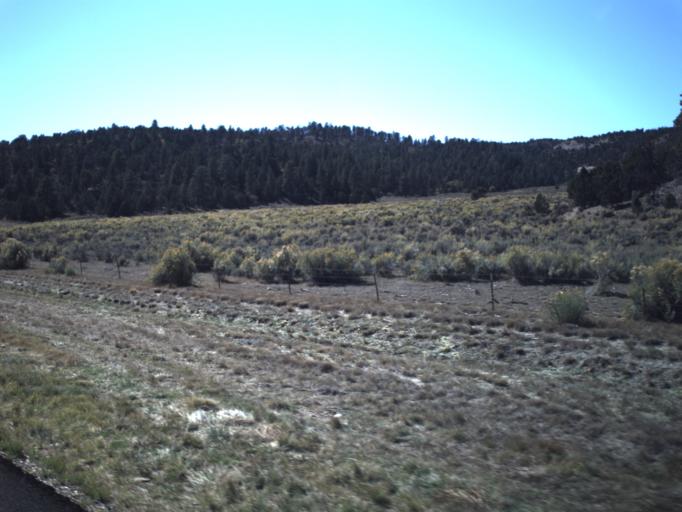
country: US
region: Utah
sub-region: Garfield County
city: Panguitch
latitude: 37.6664
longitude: -111.8313
